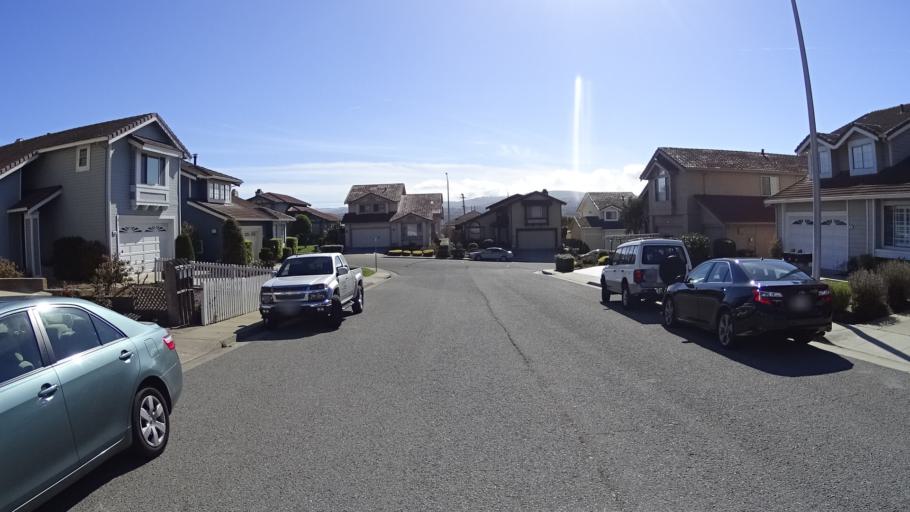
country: US
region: California
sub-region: San Mateo County
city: South San Francisco
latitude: 37.6618
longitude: -122.4287
